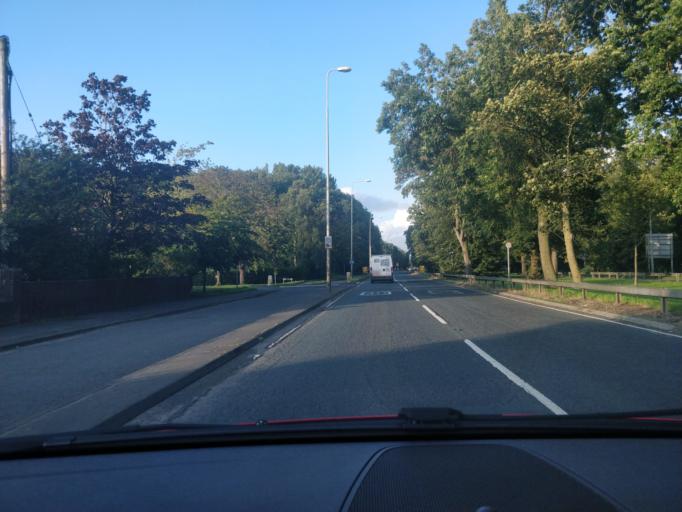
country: GB
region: England
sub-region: Lancashire
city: Preston
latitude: 53.7363
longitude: -2.7578
